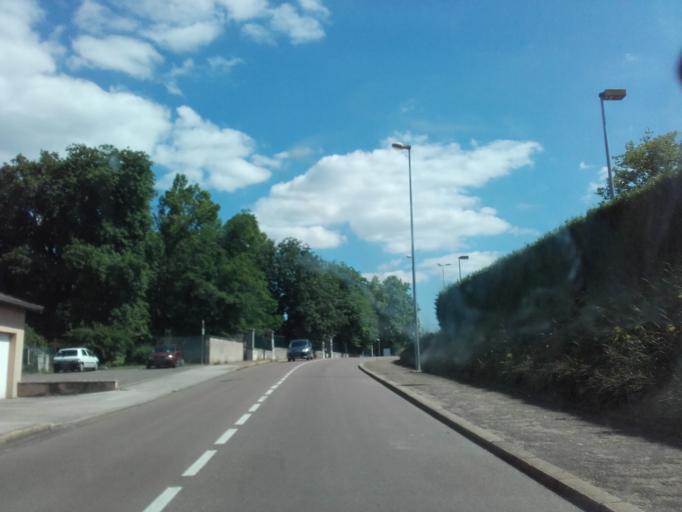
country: FR
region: Bourgogne
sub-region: Departement de Saone-et-Loire
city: Chagny
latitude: 46.9083
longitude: 4.7494
